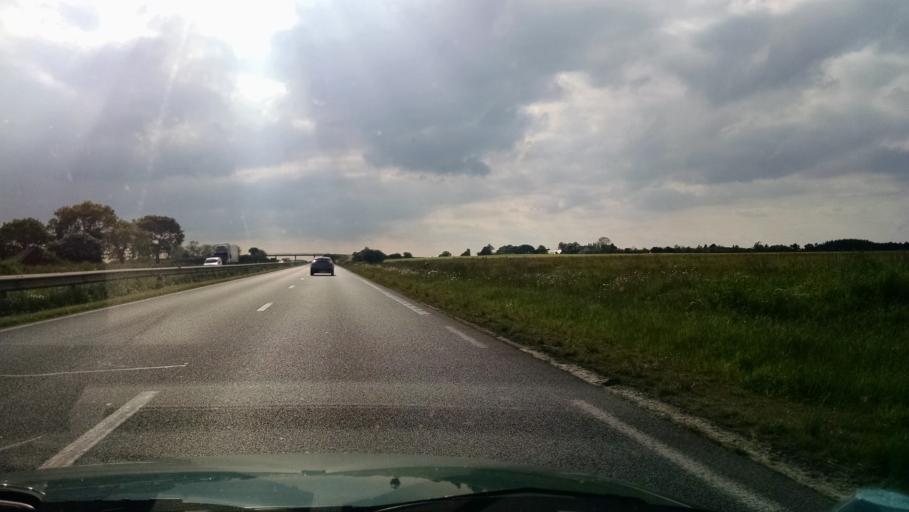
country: FR
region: Brittany
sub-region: Departement des Cotes-d'Armor
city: Pordic
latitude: 48.5451
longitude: -2.8175
